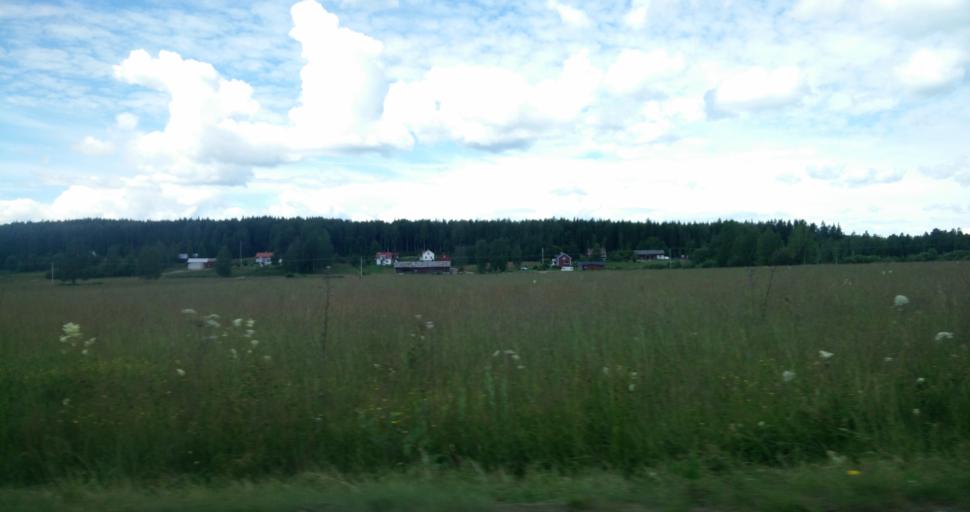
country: SE
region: Vaermland
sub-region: Hagfors Kommun
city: Ekshaerad
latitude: 60.1304
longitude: 13.4579
